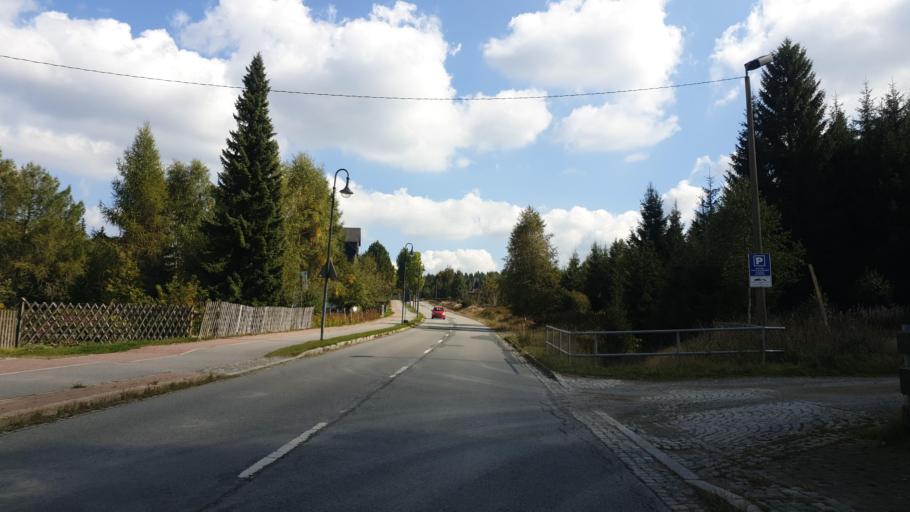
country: DE
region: Saxony
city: Johanngeorgenstadt
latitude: 50.4425
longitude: 12.6805
